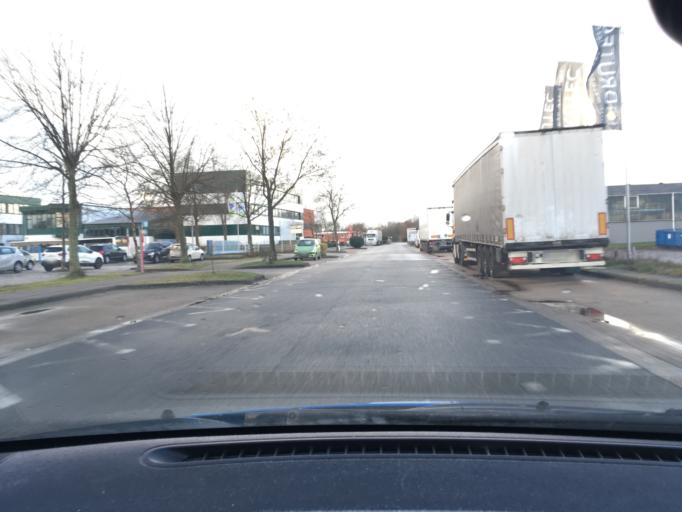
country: DE
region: Lower Saxony
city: Seevetal
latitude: 53.3872
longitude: 10.0057
